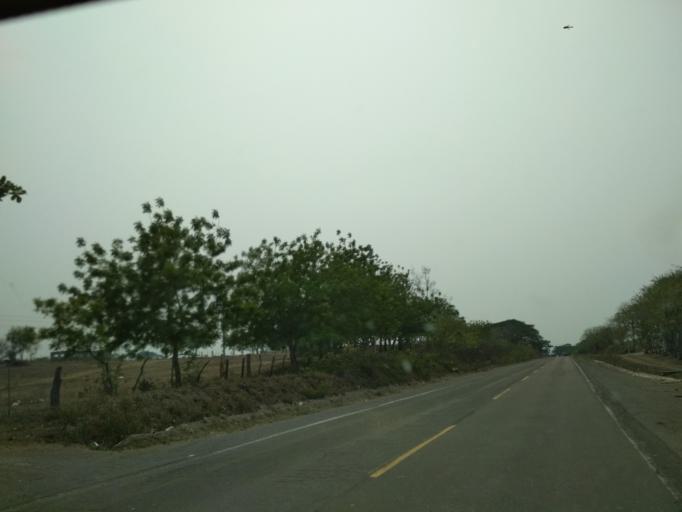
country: MX
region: Veracruz
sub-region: Veracruz
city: Delfino Victoria (Santa Fe)
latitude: 19.2021
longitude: -96.3097
